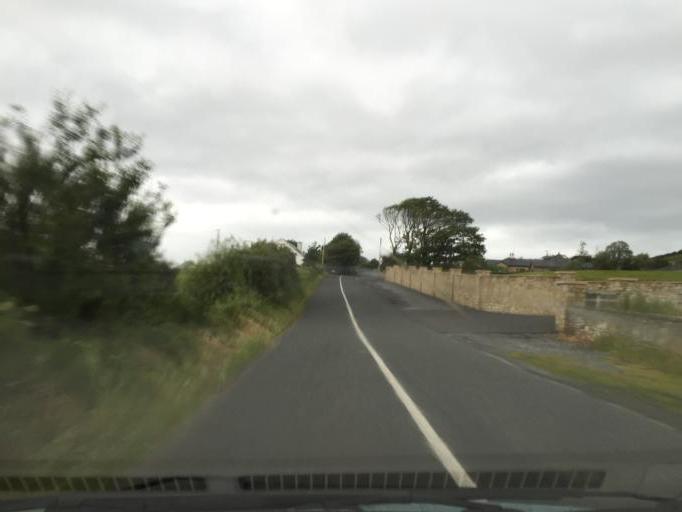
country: IE
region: Connaught
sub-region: Sligo
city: Strandhill
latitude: 54.2591
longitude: -8.5972
